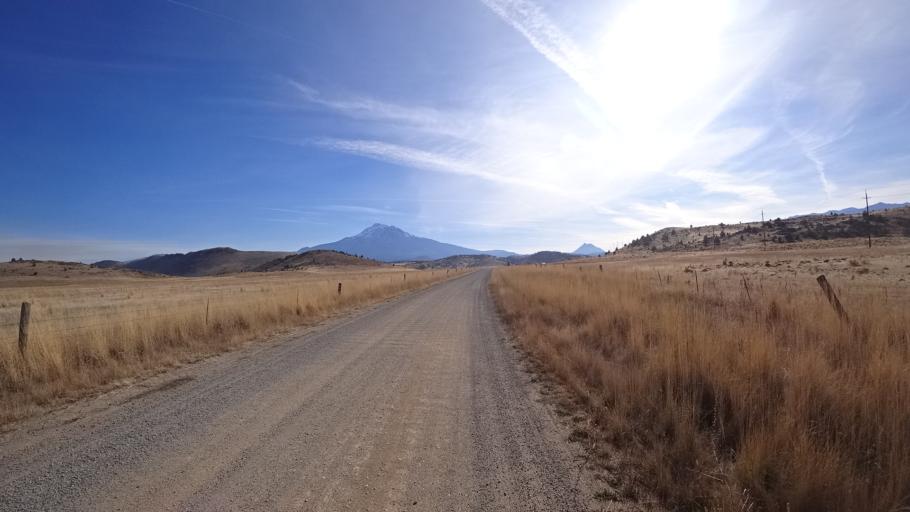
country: US
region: California
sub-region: Siskiyou County
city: Weed
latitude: 41.5108
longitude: -122.4648
